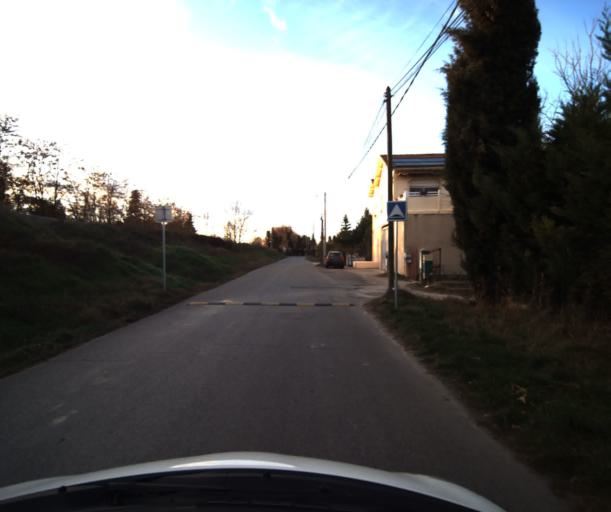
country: FR
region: Provence-Alpes-Cote d'Azur
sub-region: Departement du Vaucluse
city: Pertuis
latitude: 43.6867
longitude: 5.4978
